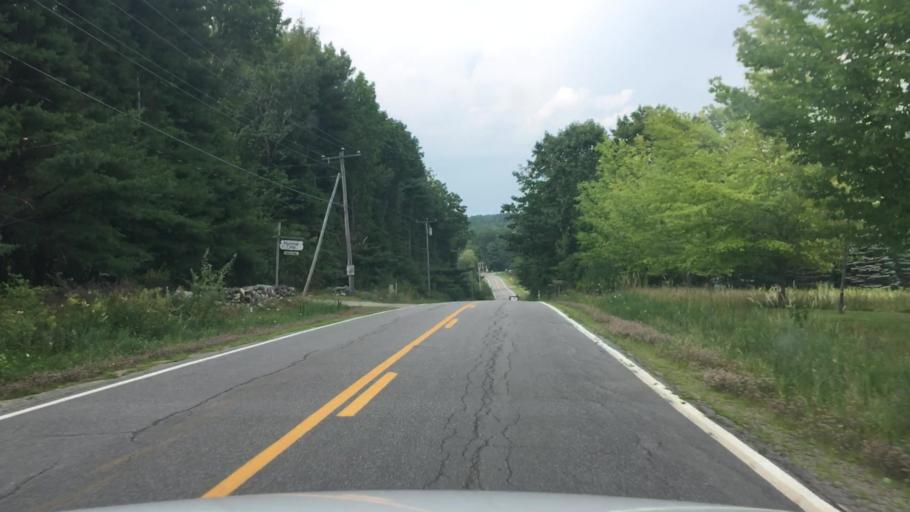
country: US
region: Maine
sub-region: Knox County
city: Washington
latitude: 44.2853
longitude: -69.3657
